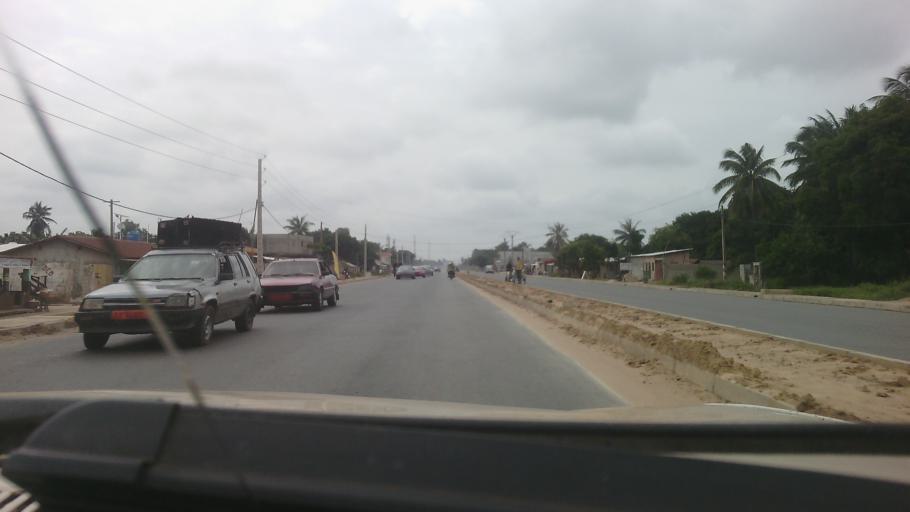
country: BJ
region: Atlantique
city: Hevie
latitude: 6.3843
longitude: 2.1965
